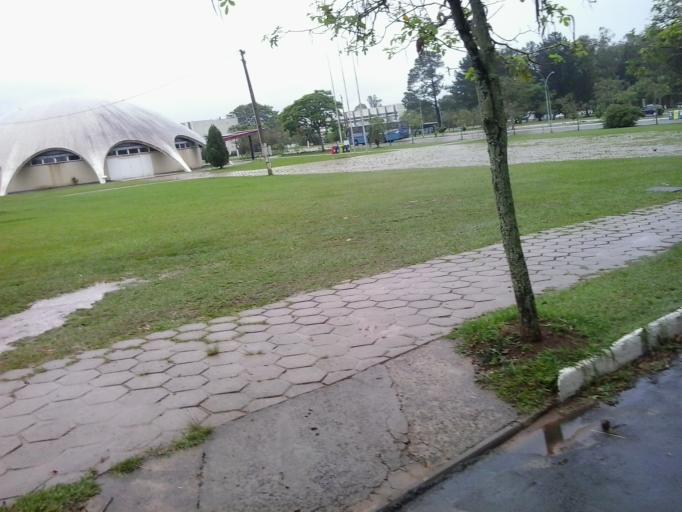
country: BR
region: Rio Grande do Sul
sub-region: Santa Maria
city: Santa Maria
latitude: -29.7209
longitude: -53.7175
